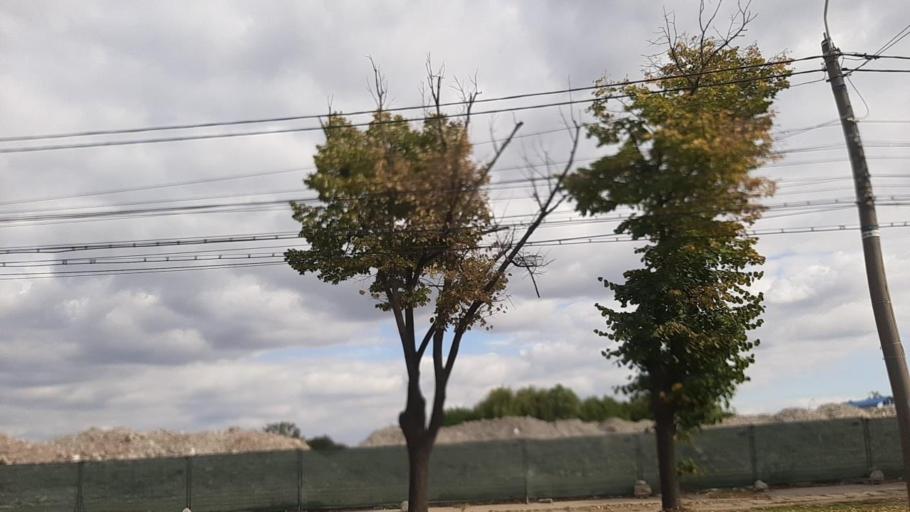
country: RO
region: Galati
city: Galati
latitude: 45.4500
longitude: 28.0349
